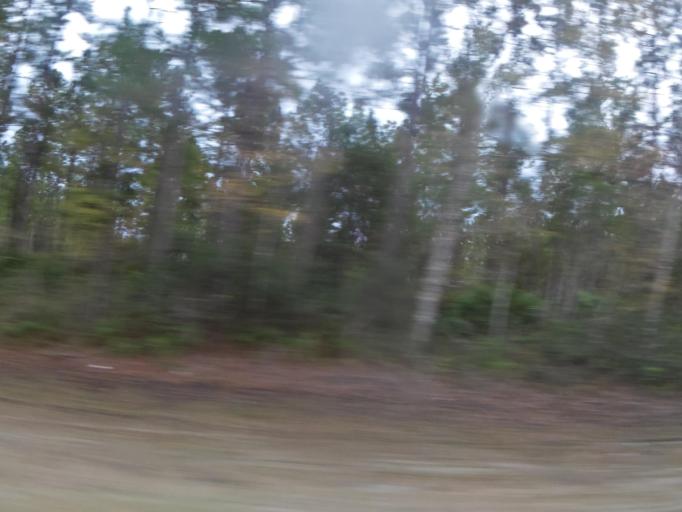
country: US
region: Georgia
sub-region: Charlton County
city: Folkston
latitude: 30.7869
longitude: -82.0449
